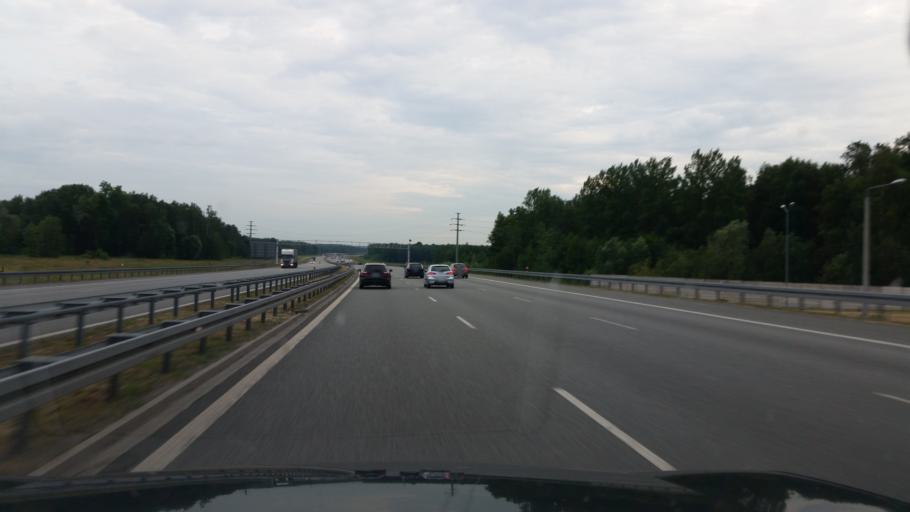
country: PL
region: Silesian Voivodeship
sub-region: Powiat gliwicki
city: Gieraltowice
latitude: 50.2117
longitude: 18.6930
